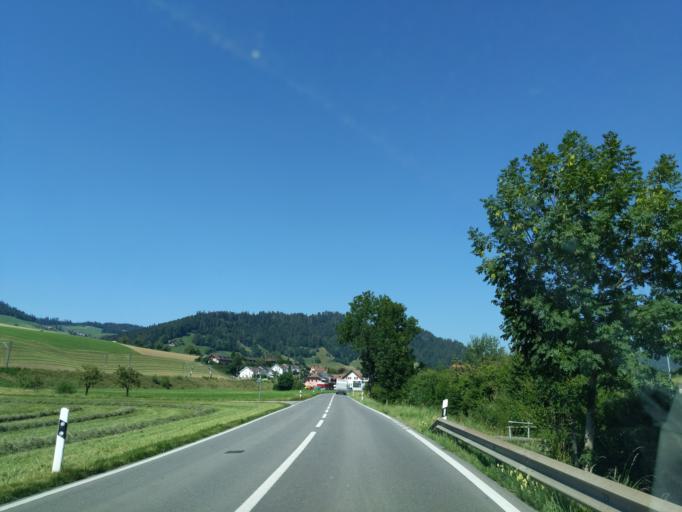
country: CH
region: Bern
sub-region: Bern-Mittelland District
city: Zaziwil
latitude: 46.8945
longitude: 7.6567
